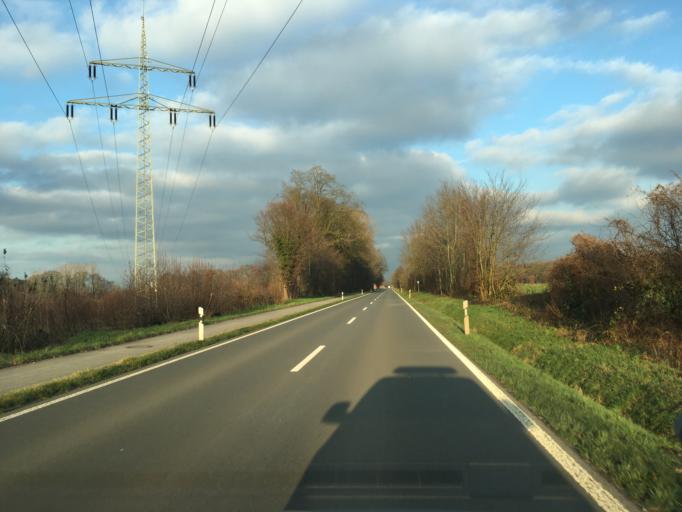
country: DE
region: North Rhine-Westphalia
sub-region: Regierungsbezirk Munster
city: Ahaus
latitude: 52.1449
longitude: 7.0126
